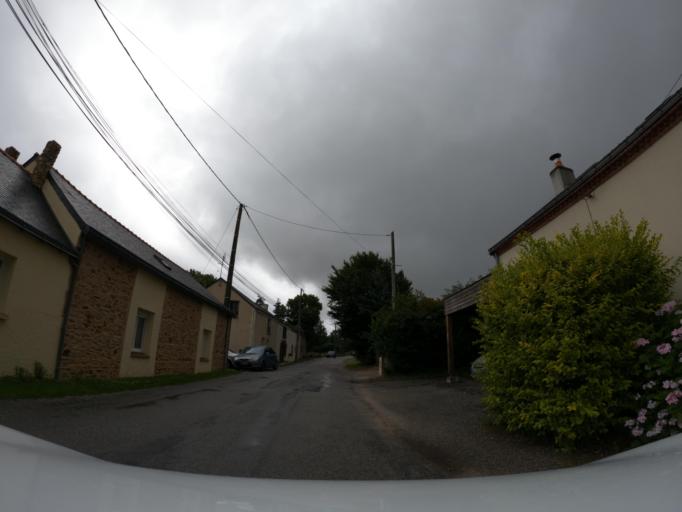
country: FR
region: Pays de la Loire
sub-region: Departement de la Loire-Atlantique
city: Saint-Mars-du-Desert
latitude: 47.3740
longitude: -1.4112
